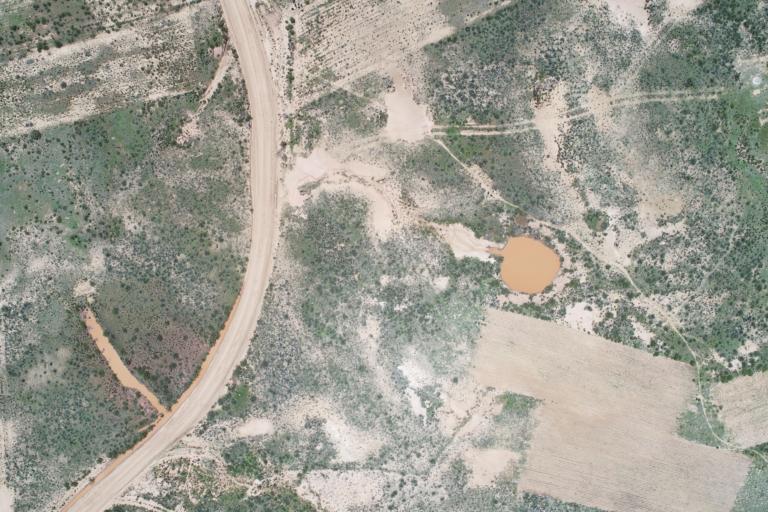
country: BO
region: La Paz
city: Curahuara de Carangas
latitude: -17.3303
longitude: -68.5153
